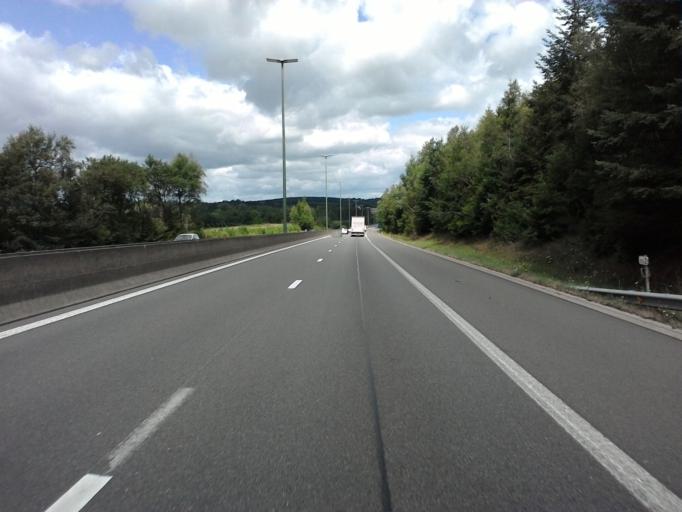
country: BE
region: Wallonia
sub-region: Province du Luxembourg
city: Leglise
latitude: 49.7880
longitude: 5.5310
